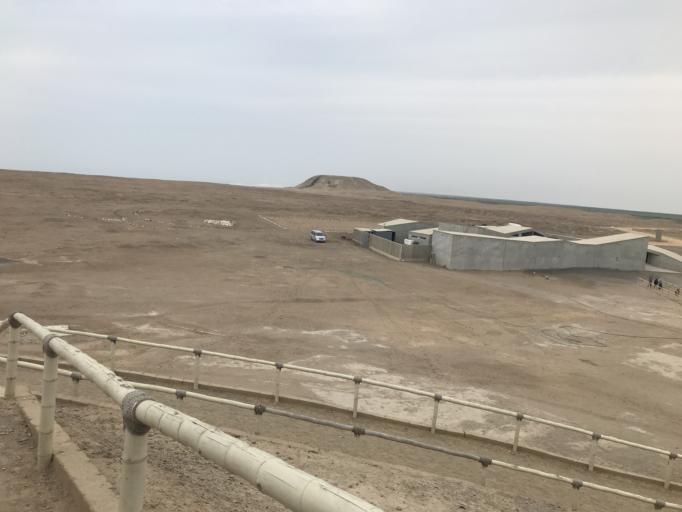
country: PE
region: La Libertad
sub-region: Ascope
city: Santiago de Cao
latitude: -7.9148
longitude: -79.3035
